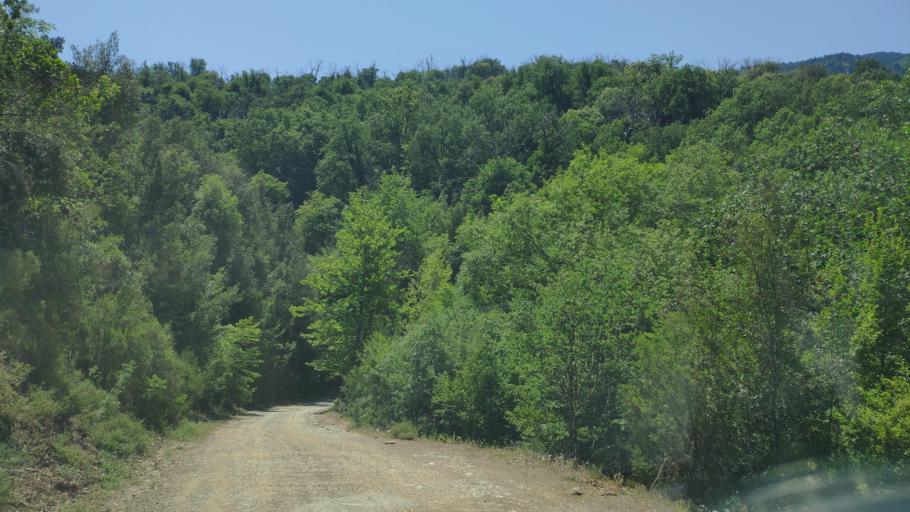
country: GR
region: Epirus
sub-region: Nomos Artas
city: Ano Kalentini
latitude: 39.1768
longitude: 21.3607
